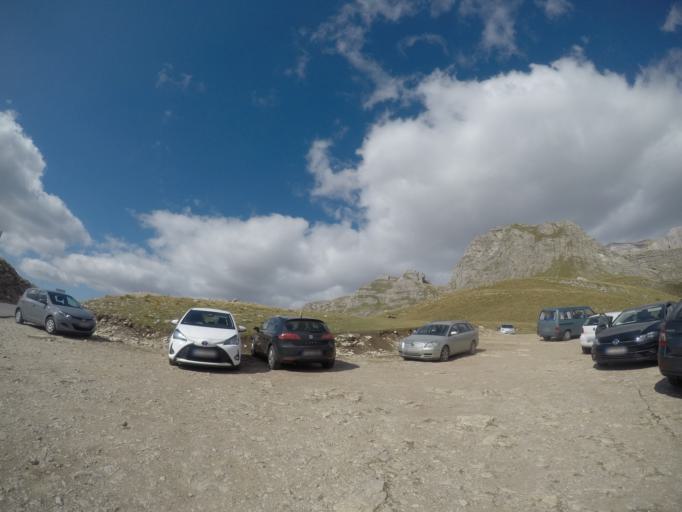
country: ME
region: Opstina Zabljak
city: Zabljak
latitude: 43.0984
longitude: 19.0510
